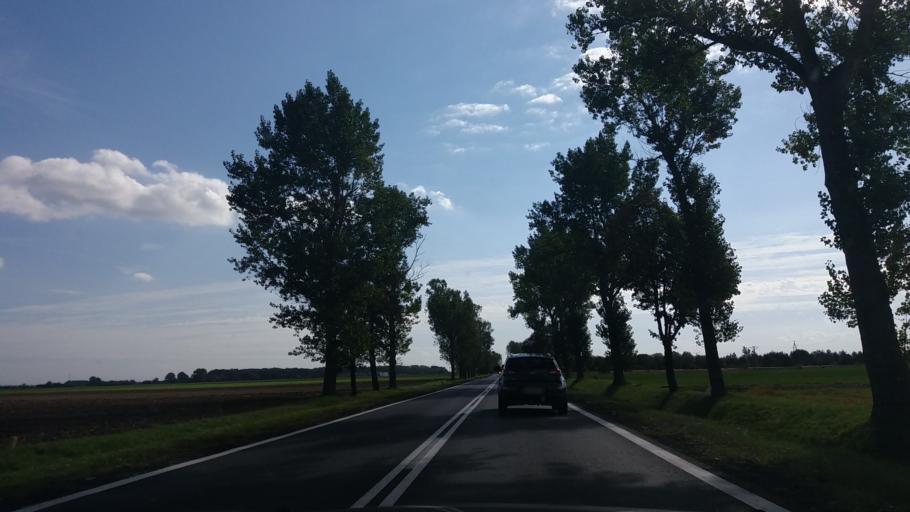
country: PL
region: Lower Silesian Voivodeship
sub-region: Powiat legnicki
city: Prochowice
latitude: 51.3255
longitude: 16.3131
